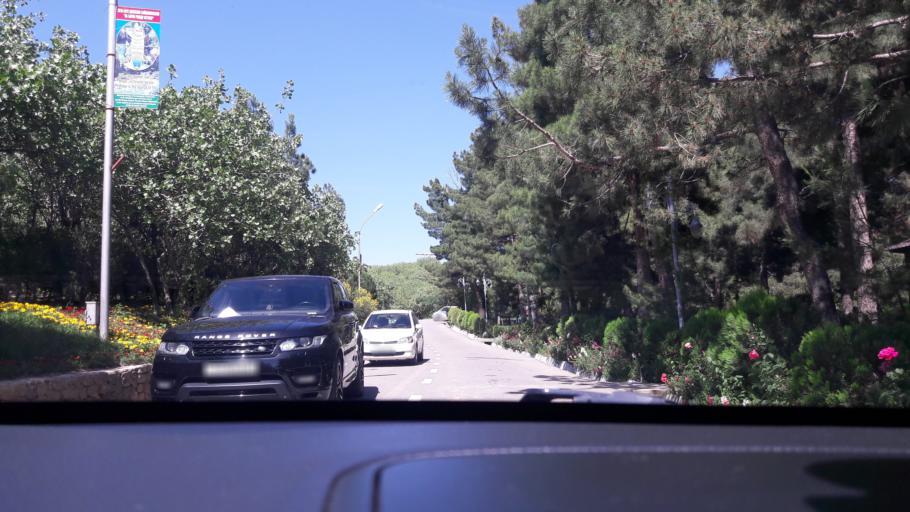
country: TJ
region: Dushanbe
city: Dushanbe
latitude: 38.5821
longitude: 68.8129
